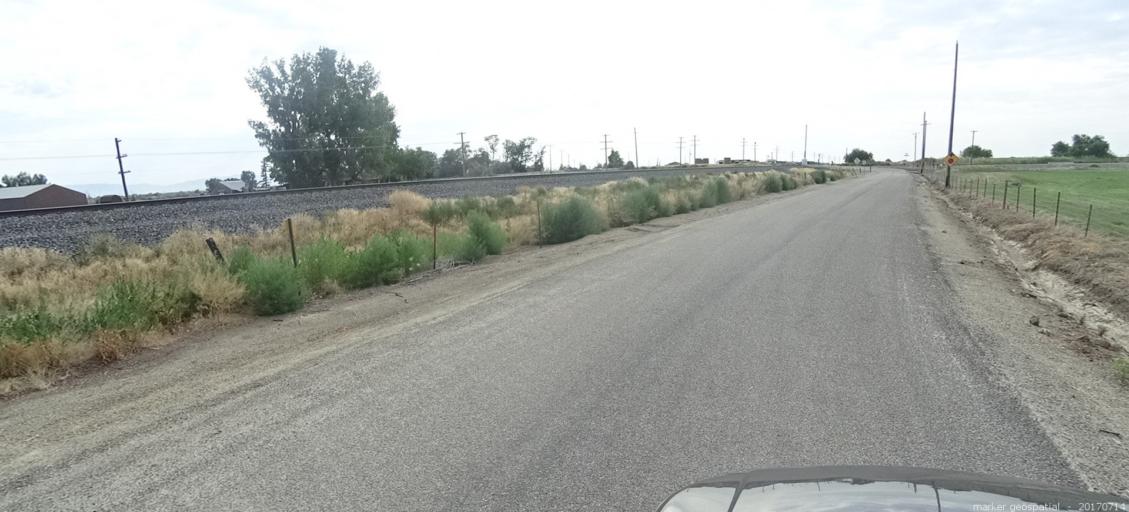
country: US
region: Idaho
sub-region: Ada County
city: Kuna
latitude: 43.4593
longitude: -116.3564
